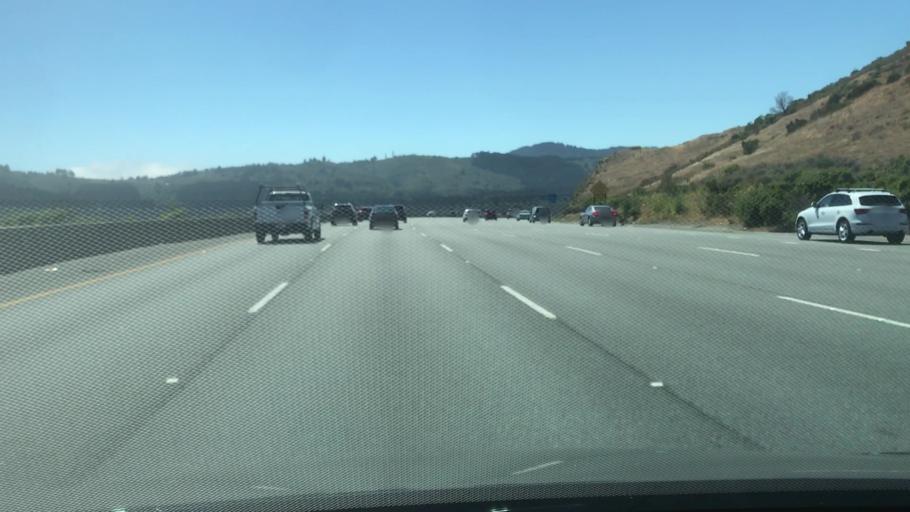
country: US
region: California
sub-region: San Mateo County
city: Highlands-Baywood Park
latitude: 37.5013
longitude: -122.3251
